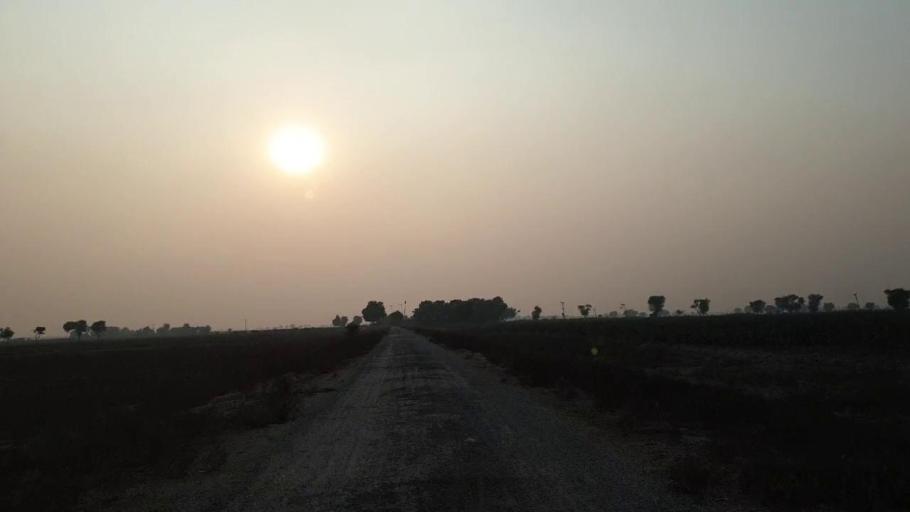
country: PK
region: Sindh
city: Bhan
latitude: 26.5065
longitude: 67.7152
